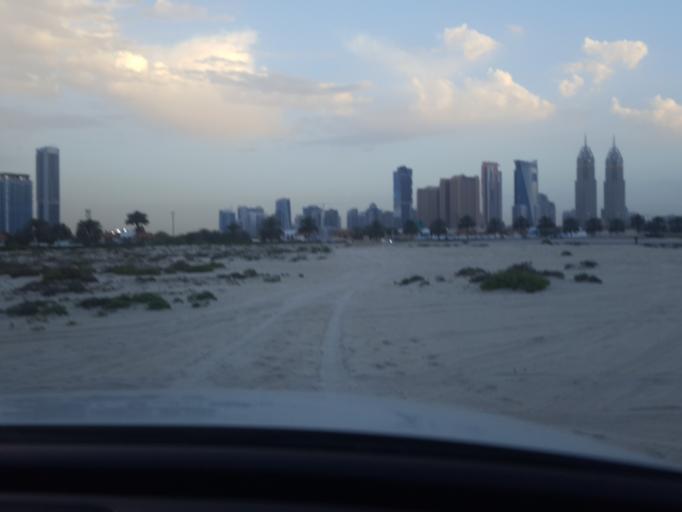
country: AE
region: Dubai
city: Dubai
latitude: 25.1167
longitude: 55.1696
